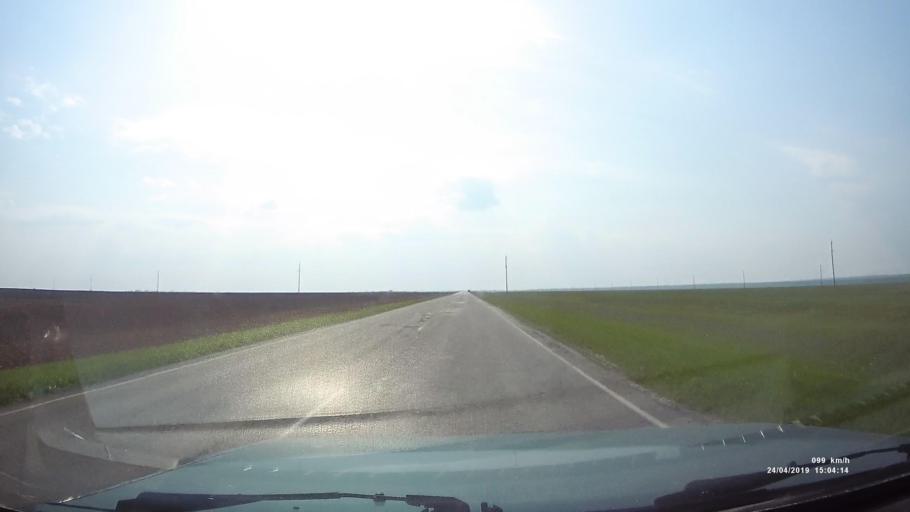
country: RU
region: Rostov
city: Remontnoye
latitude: 46.5628
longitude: 43.4748
